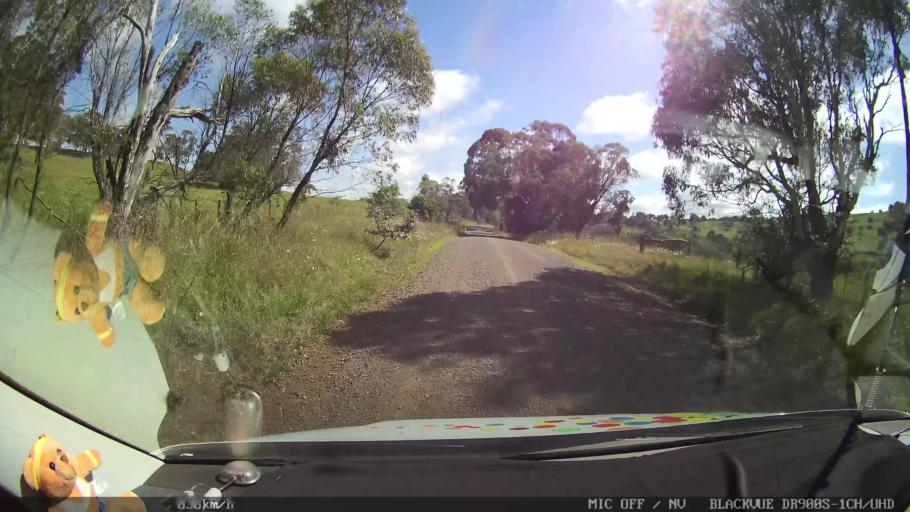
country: AU
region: New South Wales
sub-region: Guyra
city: Guyra
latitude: -29.9815
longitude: 151.6963
